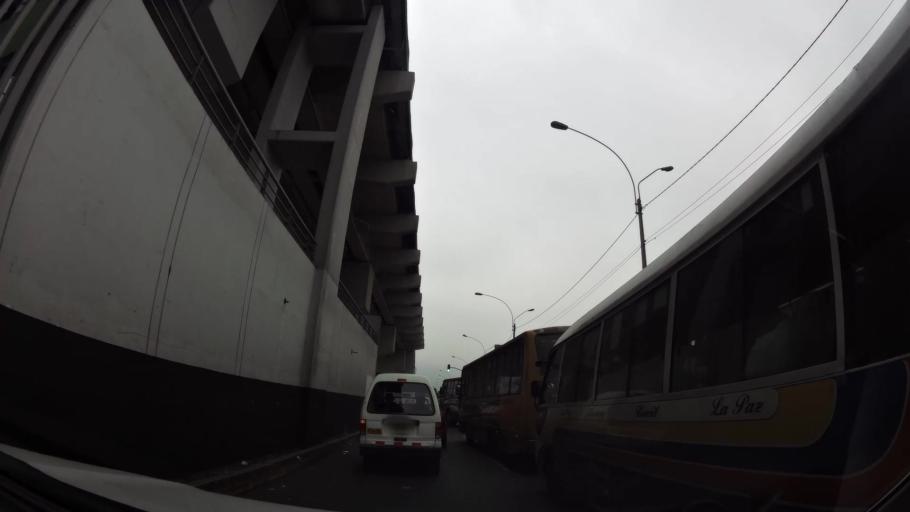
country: PE
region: Lima
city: Lima
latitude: -12.0070
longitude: -77.0052
